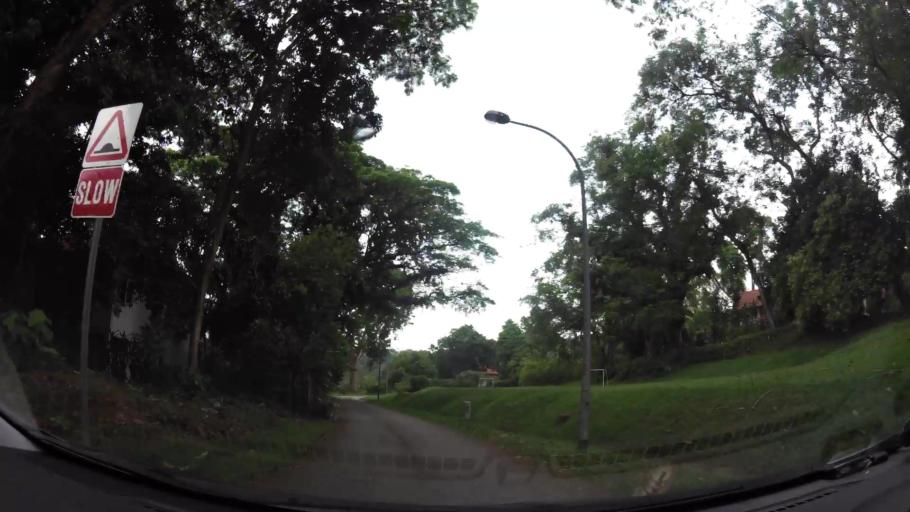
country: SG
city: Singapore
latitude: 1.2852
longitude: 103.7955
